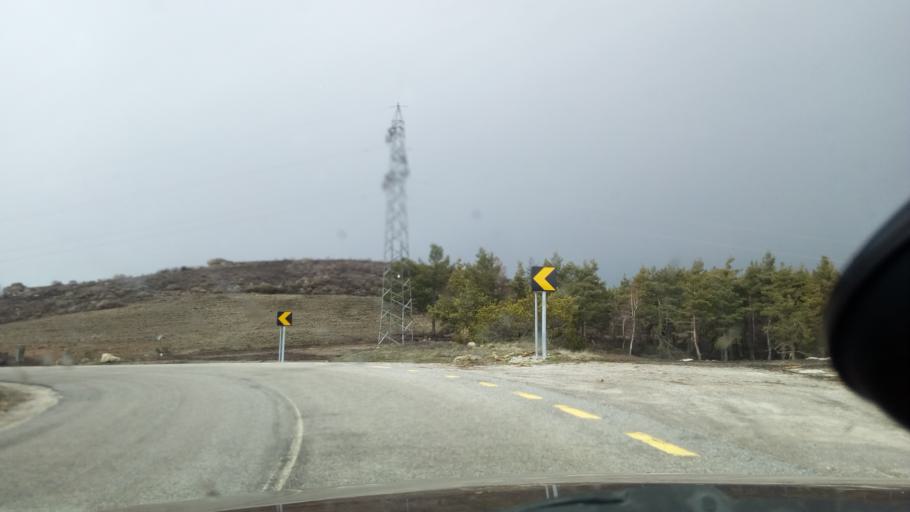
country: PT
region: Guarda
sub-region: Manteigas
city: Manteigas
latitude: 40.4226
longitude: -7.5918
